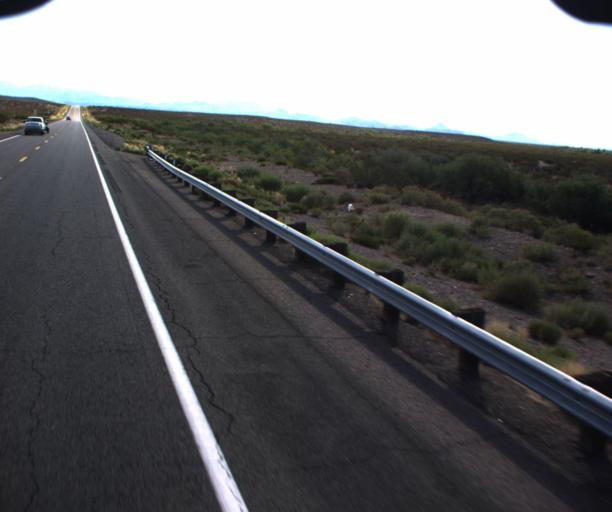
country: US
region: Arizona
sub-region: Graham County
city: Safford
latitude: 32.7940
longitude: -109.5446
